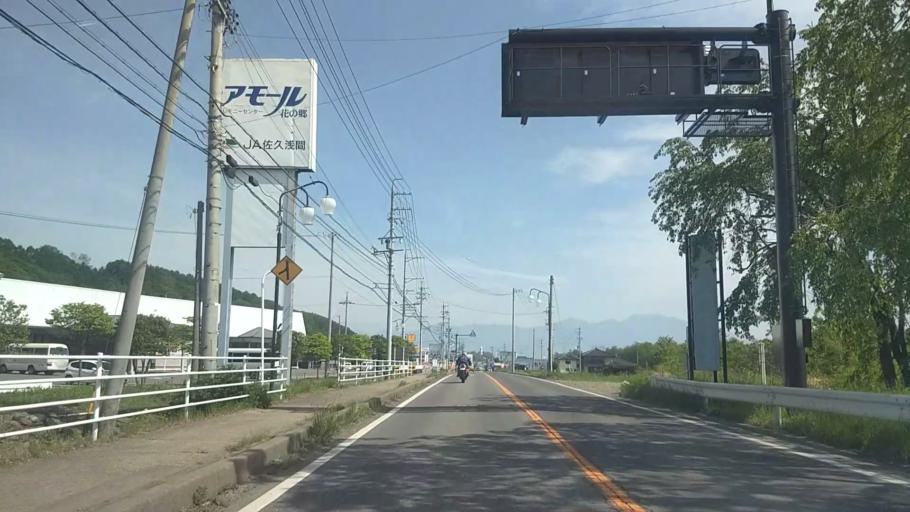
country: JP
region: Nagano
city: Saku
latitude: 36.1702
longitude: 138.4859
